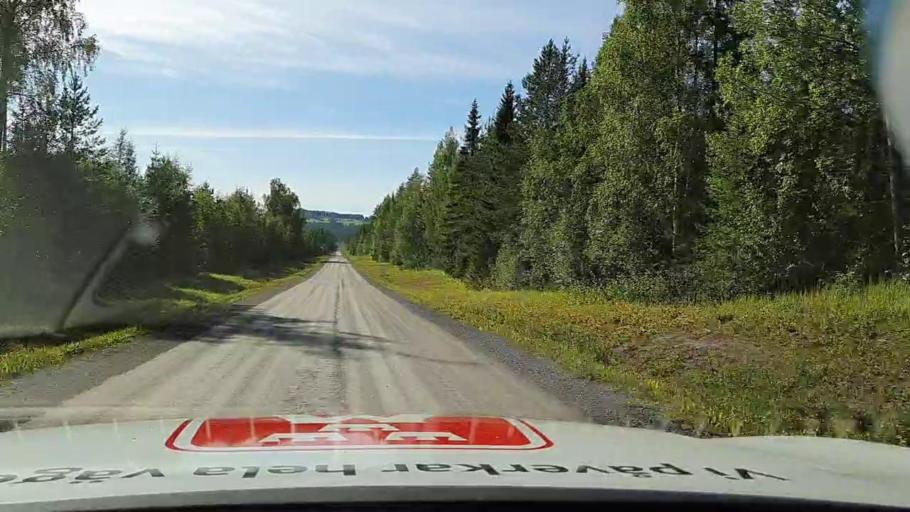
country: SE
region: Jaemtland
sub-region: OEstersunds Kommun
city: Lit
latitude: 63.6790
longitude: 14.7891
